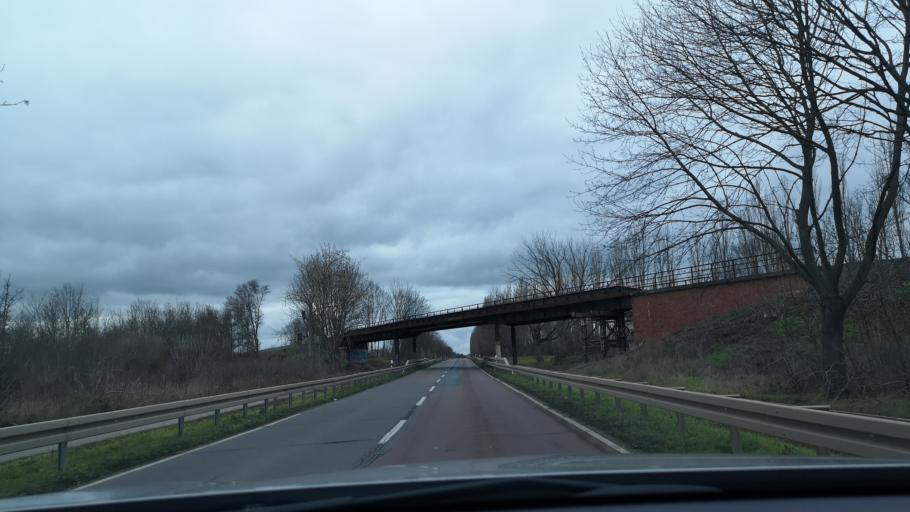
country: DE
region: Saxony-Anhalt
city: Braunsbedra
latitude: 51.2858
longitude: 11.8682
